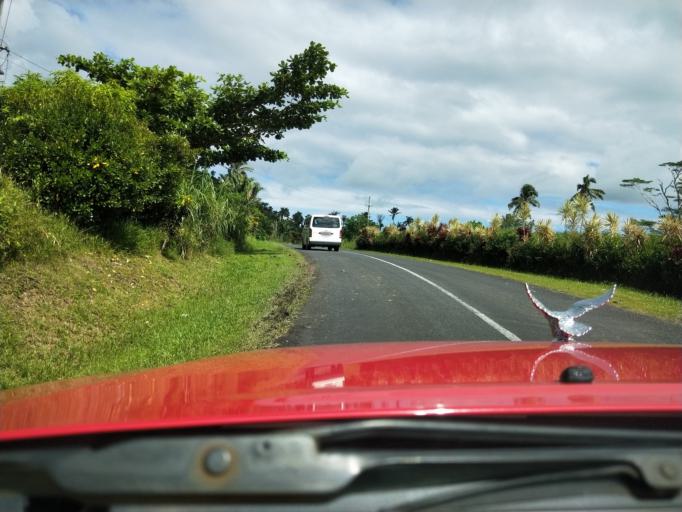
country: WS
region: Va`a-o-Fonoti
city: Samamea
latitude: -13.9649
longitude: -171.5818
